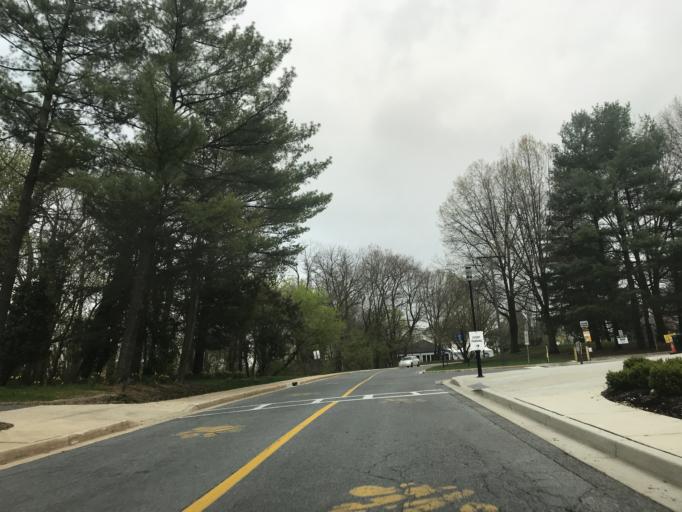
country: US
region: Maryland
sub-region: Baltimore County
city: Towson
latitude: 39.3873
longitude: -76.6154
